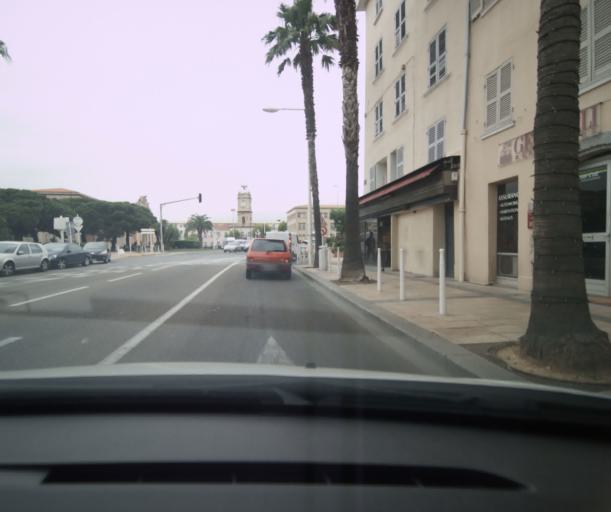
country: FR
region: Provence-Alpes-Cote d'Azur
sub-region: Departement du Var
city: Toulon
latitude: 43.1214
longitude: 5.9295
